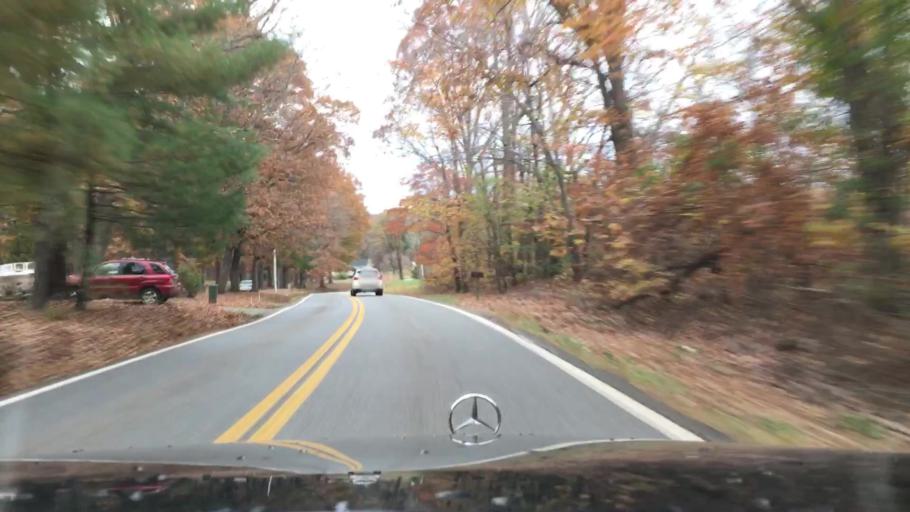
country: US
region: Virginia
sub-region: Campbell County
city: Timberlake
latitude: 37.2350
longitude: -79.2804
